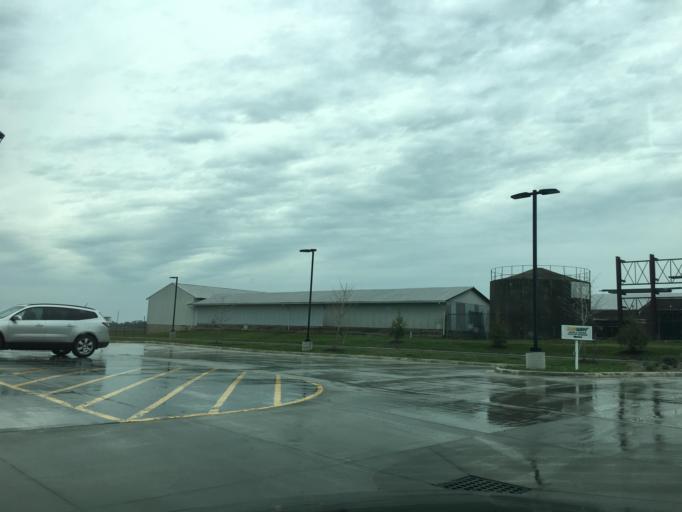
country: US
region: Ohio
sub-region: Wayne County
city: Smithville
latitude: 40.8122
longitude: -81.8447
